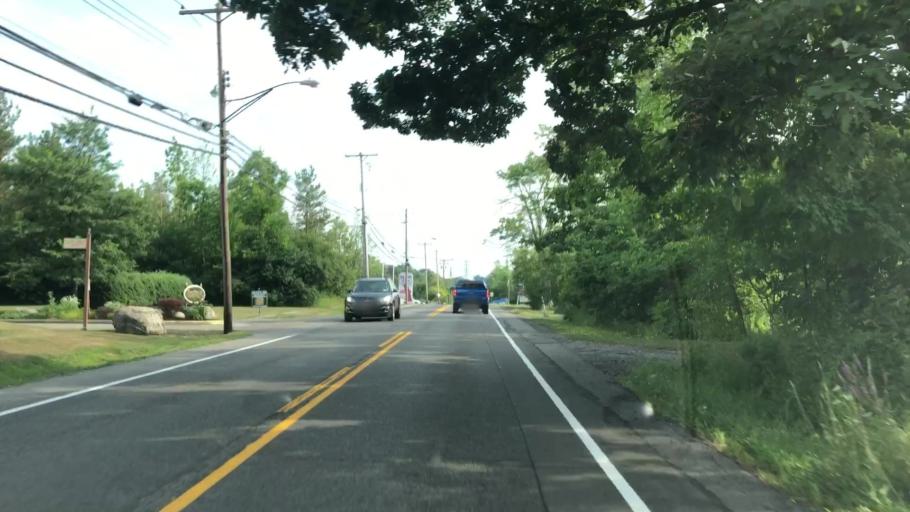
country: US
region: New York
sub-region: Erie County
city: Elma Center
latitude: 42.8365
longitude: -78.6369
